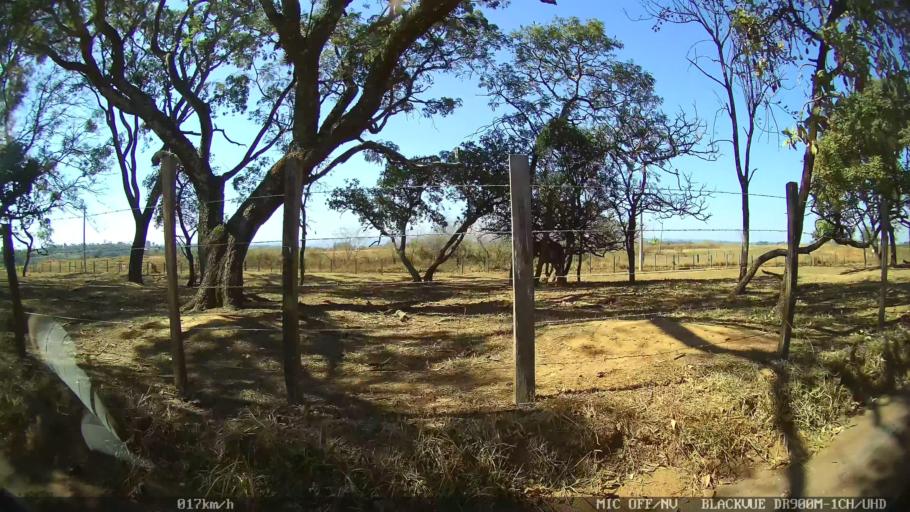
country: BR
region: Sao Paulo
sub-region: Franca
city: Franca
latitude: -20.4571
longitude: -47.4139
